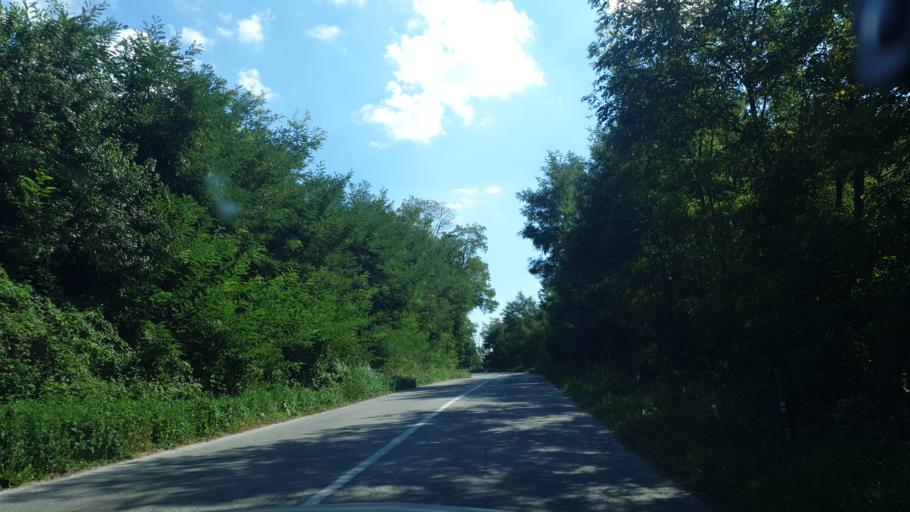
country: RS
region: Central Serbia
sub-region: Zlatiborski Okrug
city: Kosjeric
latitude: 44.0158
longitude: 20.0306
